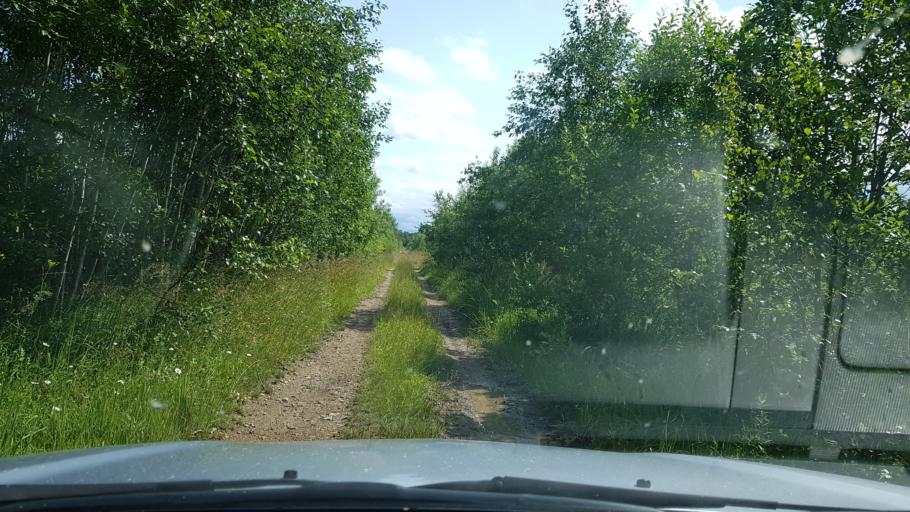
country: EE
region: Ida-Virumaa
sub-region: Sillamaee linn
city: Sillamae
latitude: 59.3656
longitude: 27.8018
